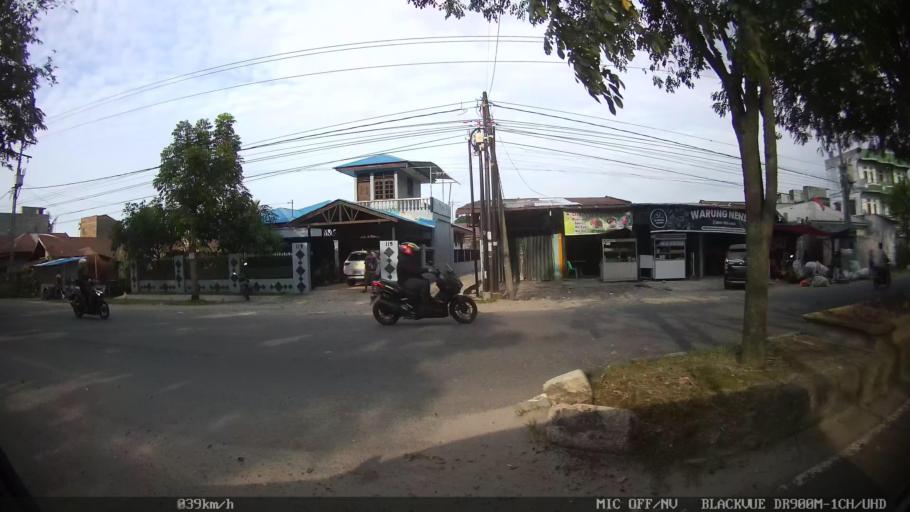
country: ID
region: North Sumatra
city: Sunggal
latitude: 3.5599
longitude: 98.6170
